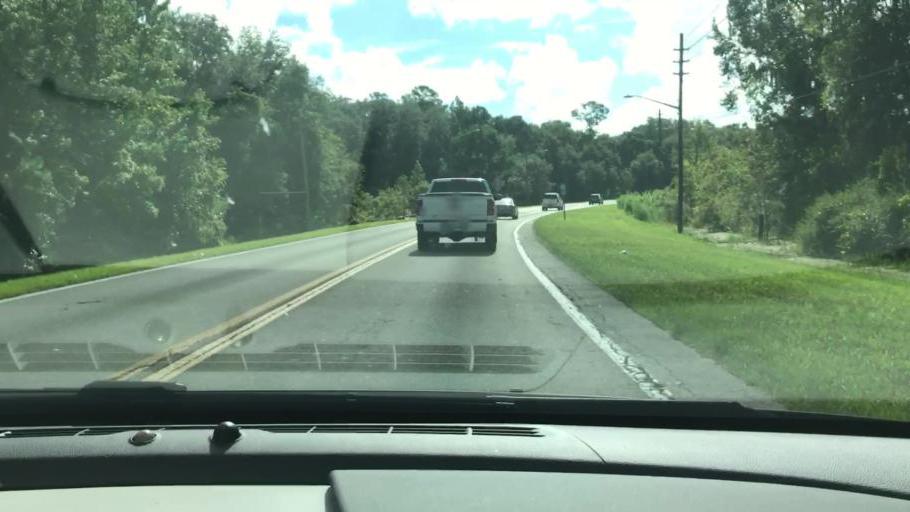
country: US
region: Florida
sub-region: Alachua County
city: Gainesville
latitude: 29.6495
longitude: -82.4048
